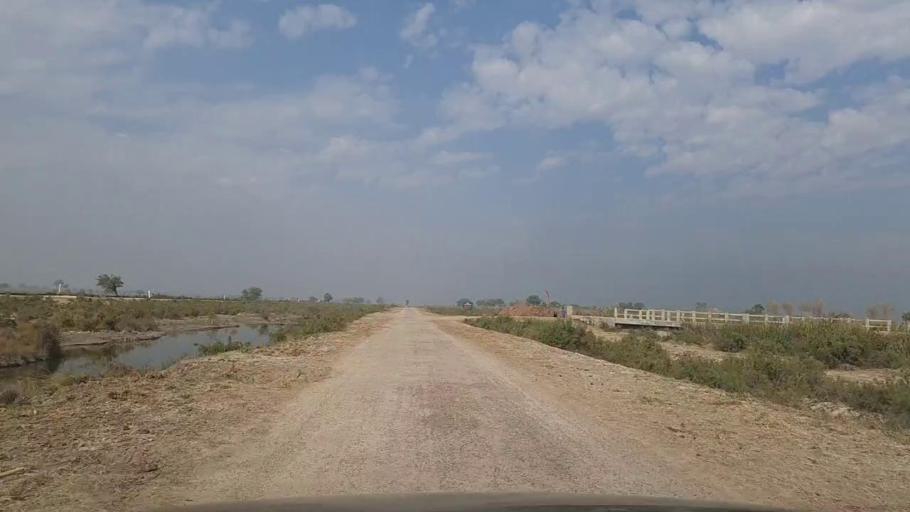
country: PK
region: Sindh
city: Daur
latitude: 26.3908
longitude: 68.3502
